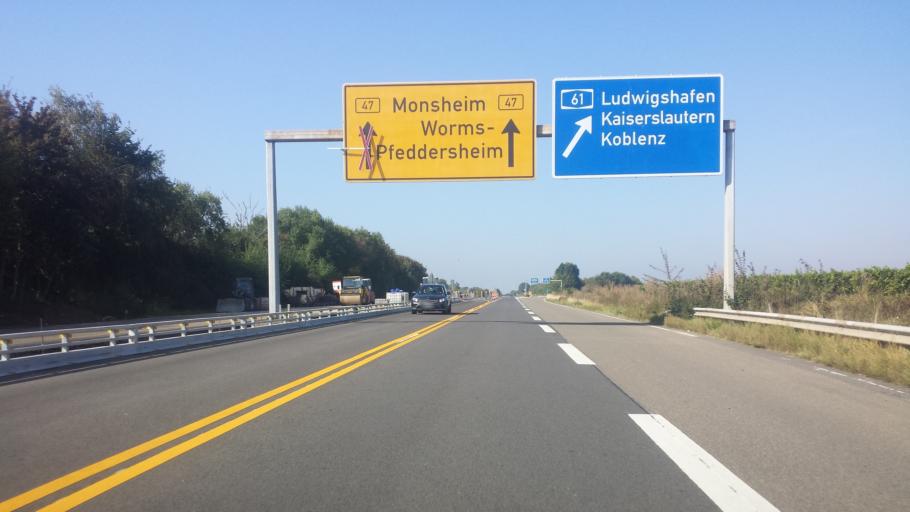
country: DE
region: Rheinland-Pfalz
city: Kleinniedesheim
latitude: 49.6242
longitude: 8.3042
